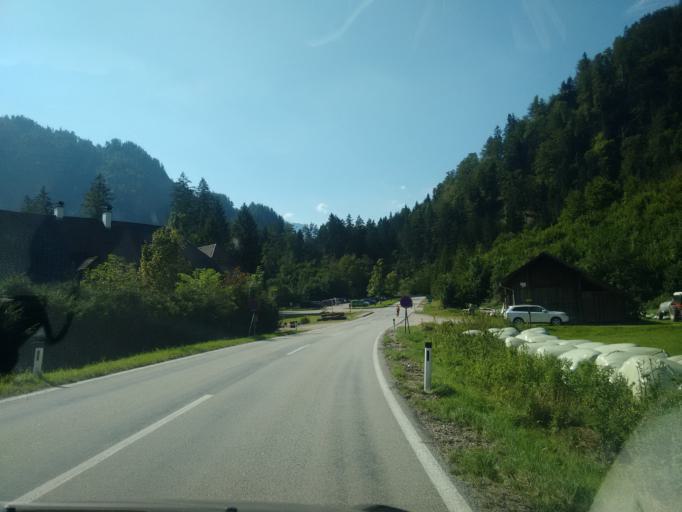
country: AT
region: Upper Austria
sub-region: Politischer Bezirk Gmunden
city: Gruenau im Almtal
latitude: 47.7789
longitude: 13.9612
